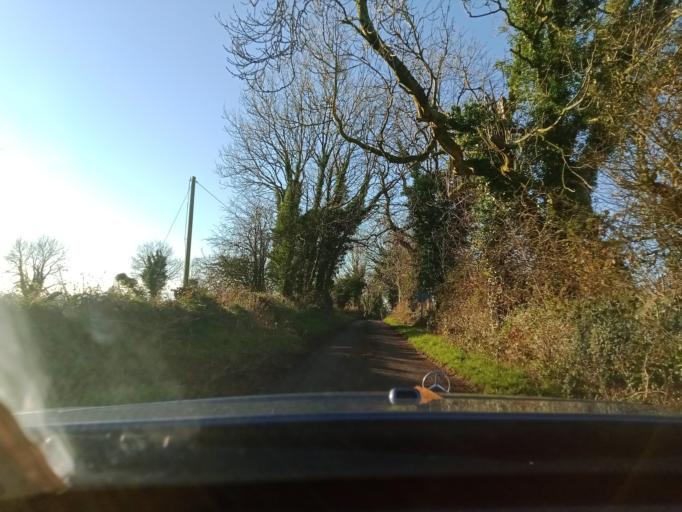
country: IE
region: Leinster
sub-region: Kilkenny
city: Callan
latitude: 52.4595
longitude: -7.4223
